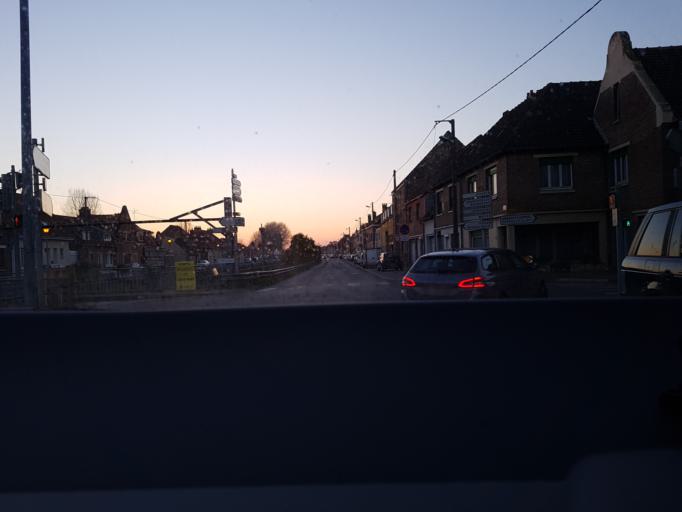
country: FR
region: Nord-Pas-de-Calais
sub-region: Departement du Nord
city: Armbouts-Cappel
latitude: 50.9654
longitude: 2.3466
